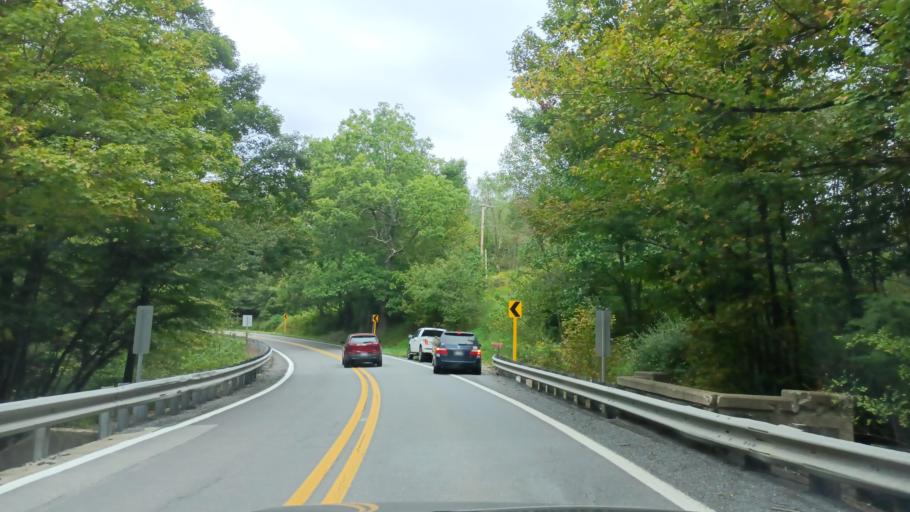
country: US
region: West Virginia
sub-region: Taylor County
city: Grafton
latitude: 39.3341
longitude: -79.8915
